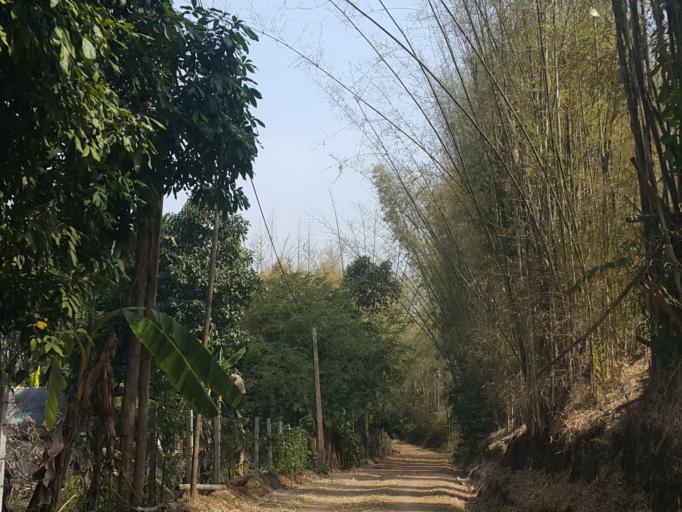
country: TH
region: Chiang Mai
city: Mae Taeng
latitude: 18.9539
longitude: 98.9165
